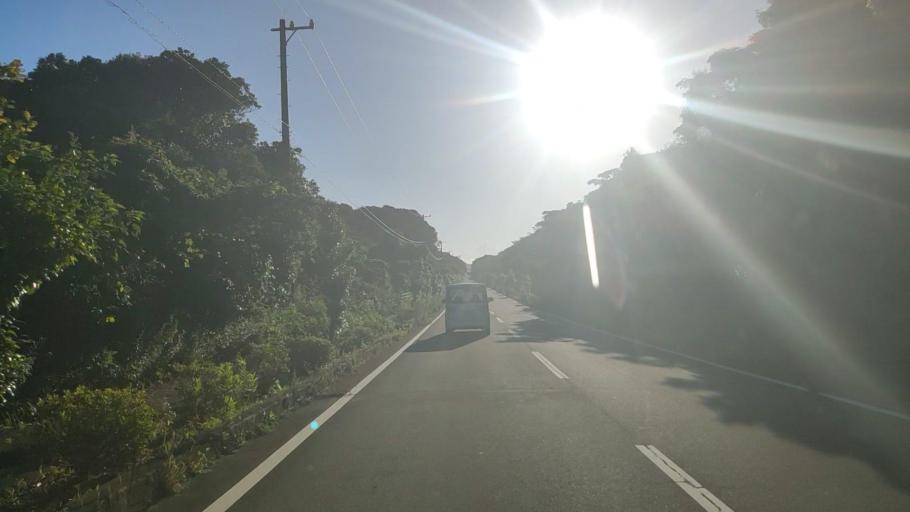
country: JP
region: Mie
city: Toba
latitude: 34.2684
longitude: 136.8054
